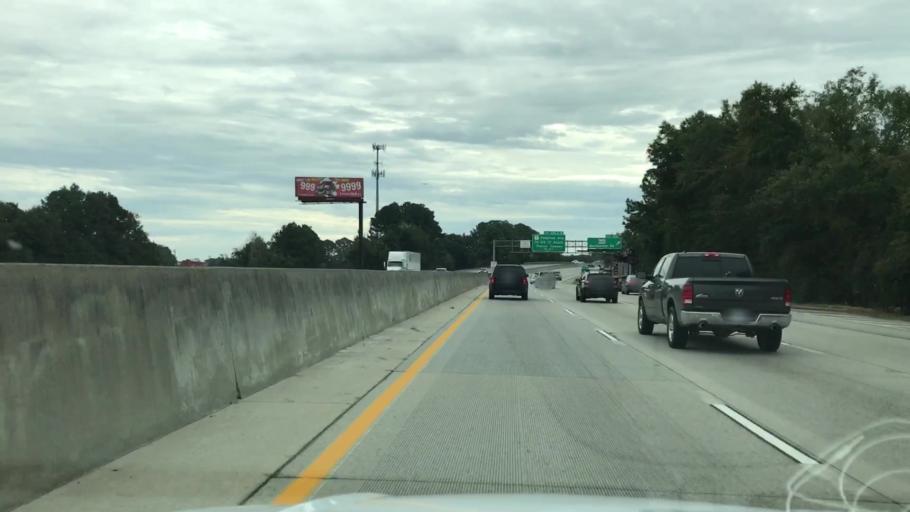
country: US
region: South Carolina
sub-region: Charleston County
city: North Charleston
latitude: 32.8563
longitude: -79.9898
